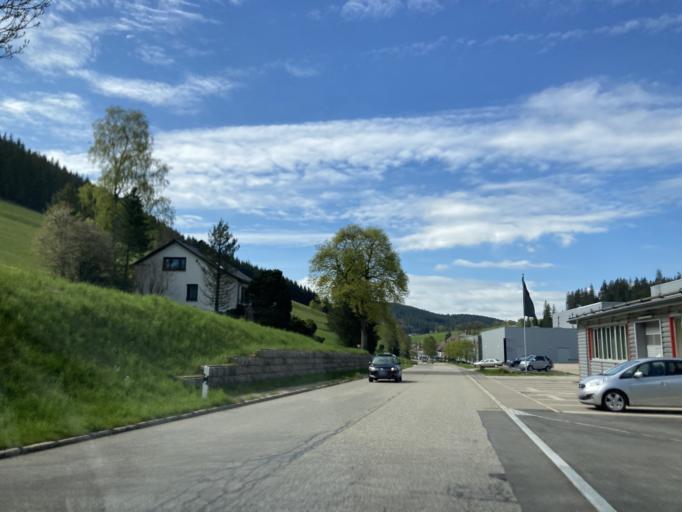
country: DE
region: Baden-Wuerttemberg
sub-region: Freiburg Region
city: Furtwangen im Schwarzwald
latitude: 48.0619
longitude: 8.2052
